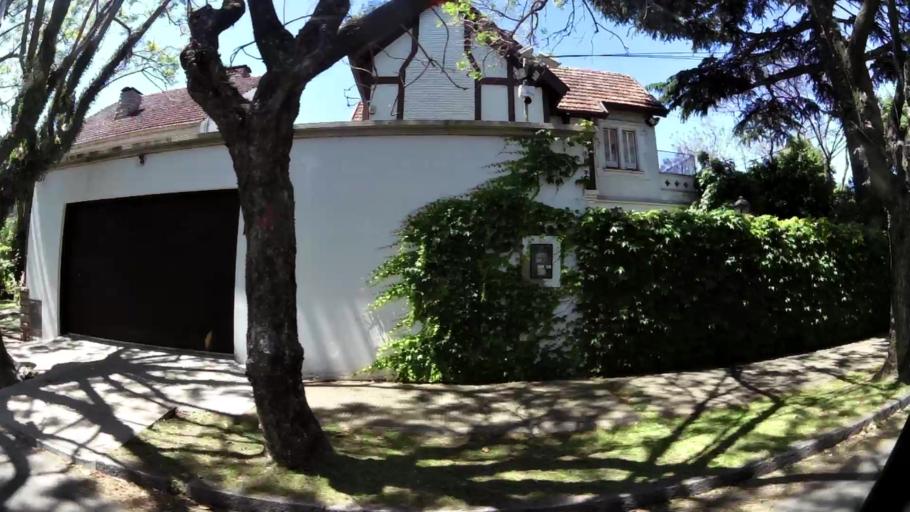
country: AR
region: Buenos Aires
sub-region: Partido de Vicente Lopez
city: Olivos
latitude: -34.5042
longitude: -58.4910
